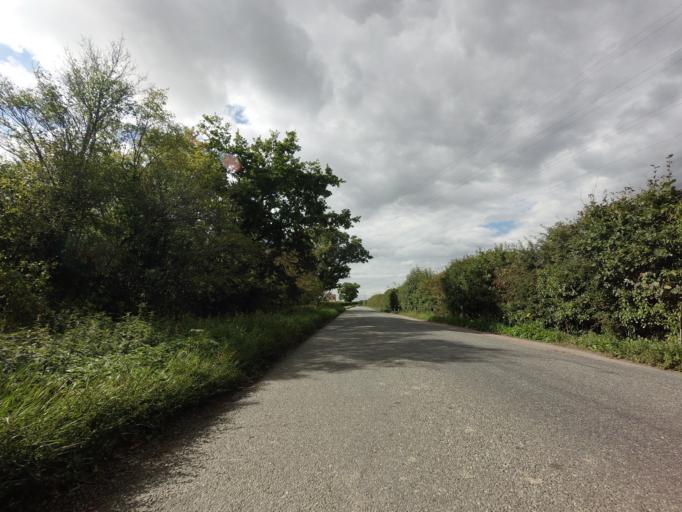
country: GB
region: England
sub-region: Kent
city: Paddock Wood
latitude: 51.1714
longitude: 0.4063
